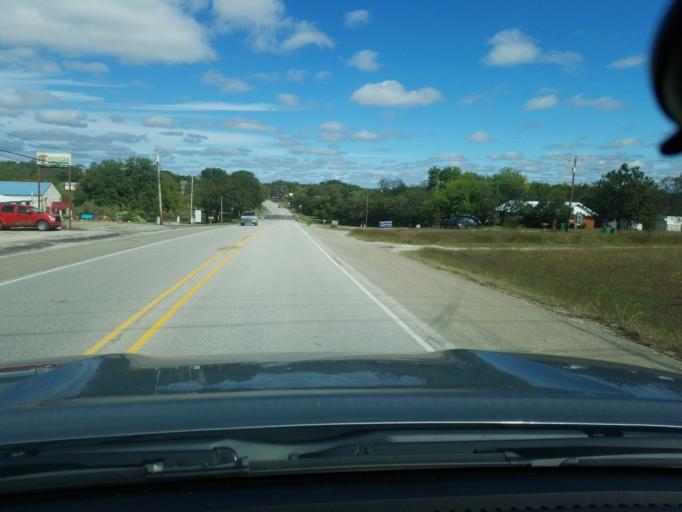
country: US
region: Texas
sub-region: Hamilton County
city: Hamilton
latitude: 31.6925
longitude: -98.1290
